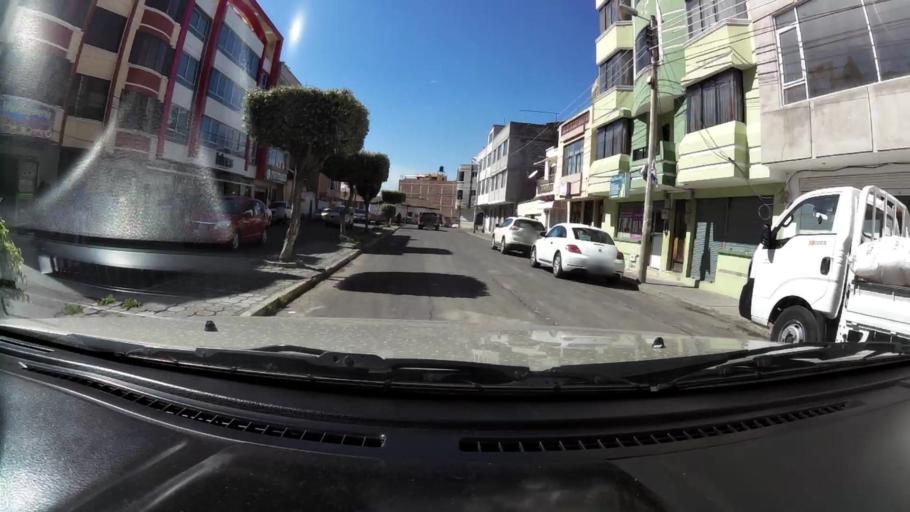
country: EC
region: Chimborazo
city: Riobamba
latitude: -1.6656
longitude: -78.6493
